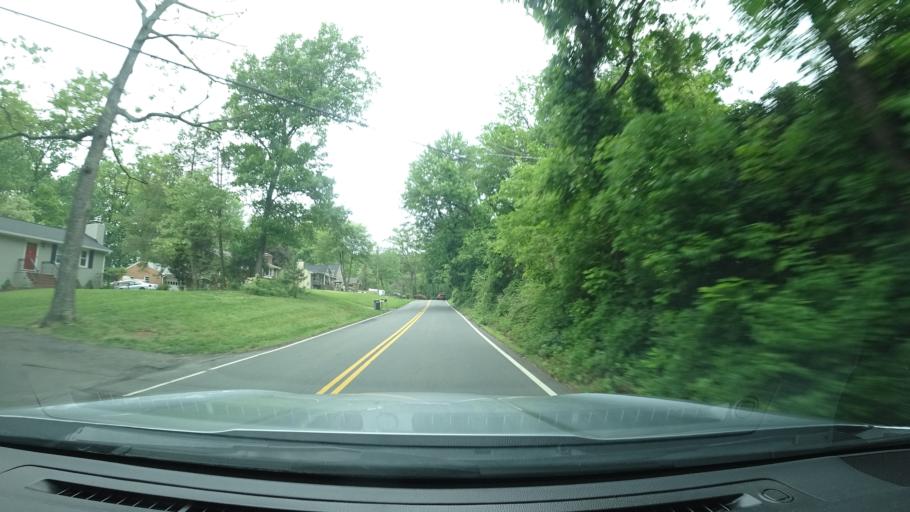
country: US
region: Virginia
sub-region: Fairfax County
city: Greenbriar
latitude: 38.8771
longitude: -77.3593
